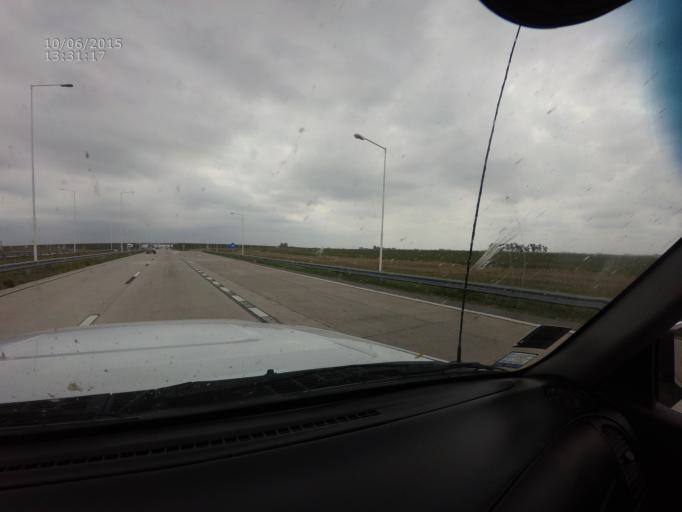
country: AR
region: Cordoba
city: Leones
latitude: -32.6315
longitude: -62.2823
